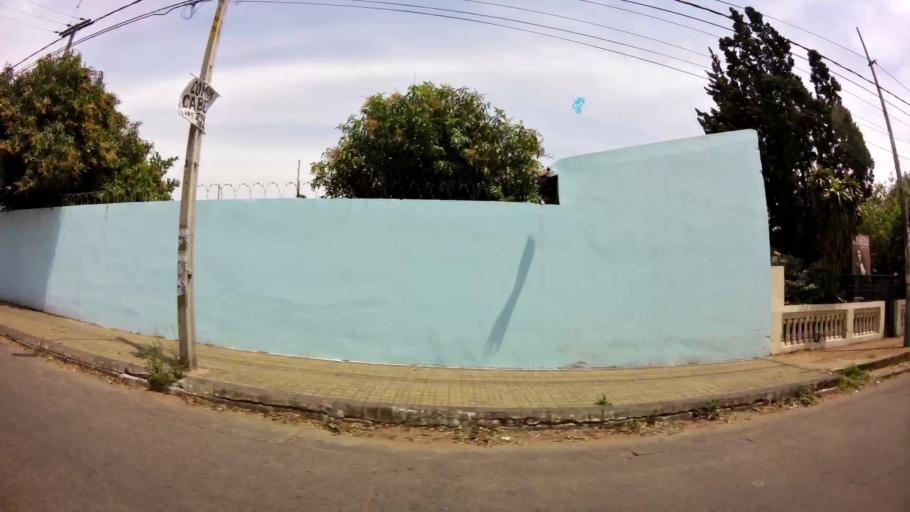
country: PY
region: Central
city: Lambare
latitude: -25.3195
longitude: -57.5996
